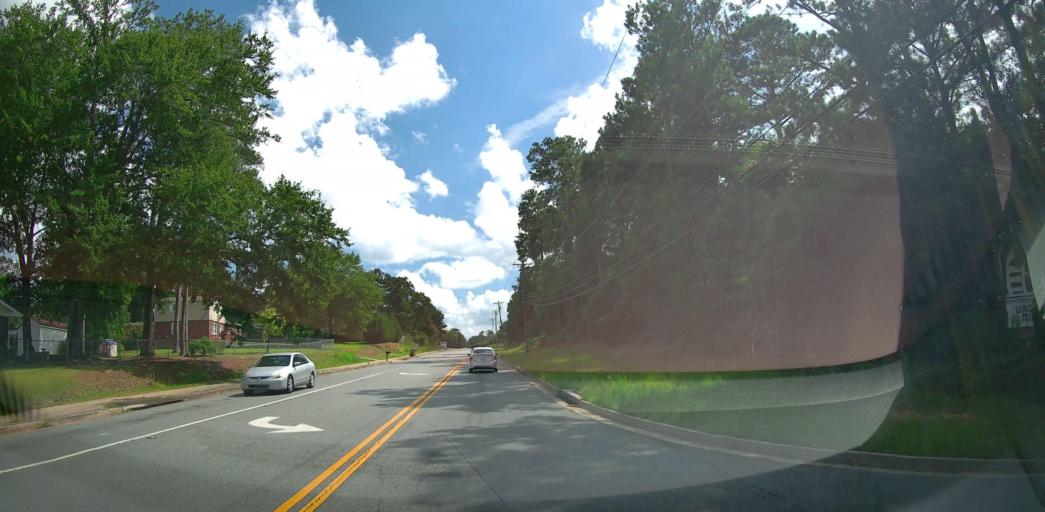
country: US
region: Georgia
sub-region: Houston County
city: Centerville
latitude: 32.6114
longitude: -83.6535
